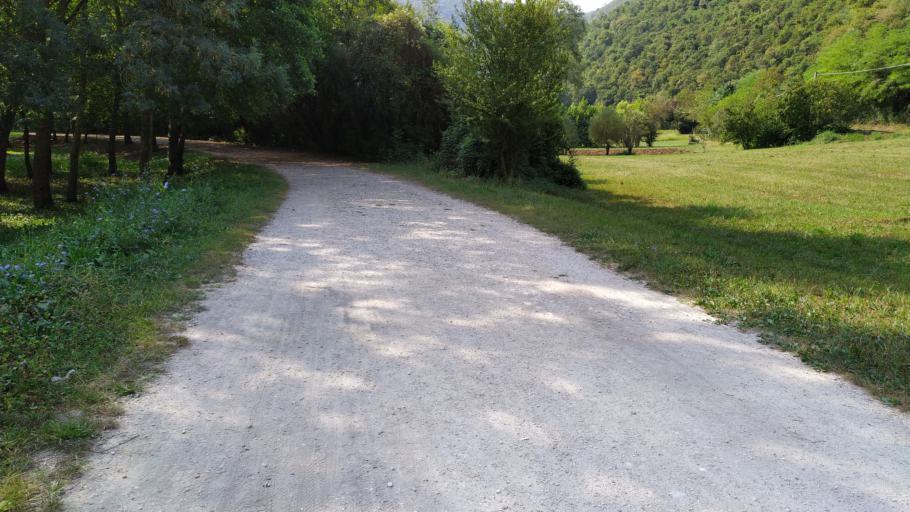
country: IT
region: Veneto
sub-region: Provincia di Vicenza
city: Arcugnano-Torri
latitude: 45.4641
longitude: 11.5402
